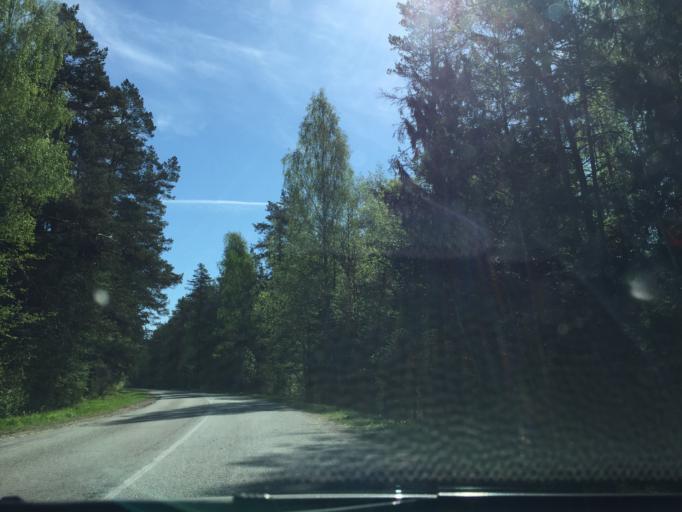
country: LV
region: Garkalne
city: Garkalne
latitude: 57.0067
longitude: 24.4771
